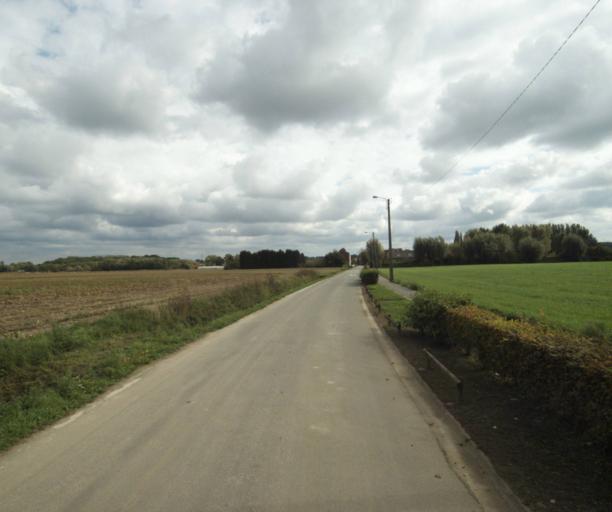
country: FR
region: Nord-Pas-de-Calais
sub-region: Departement du Nord
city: Premesques
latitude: 50.6633
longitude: 2.9393
